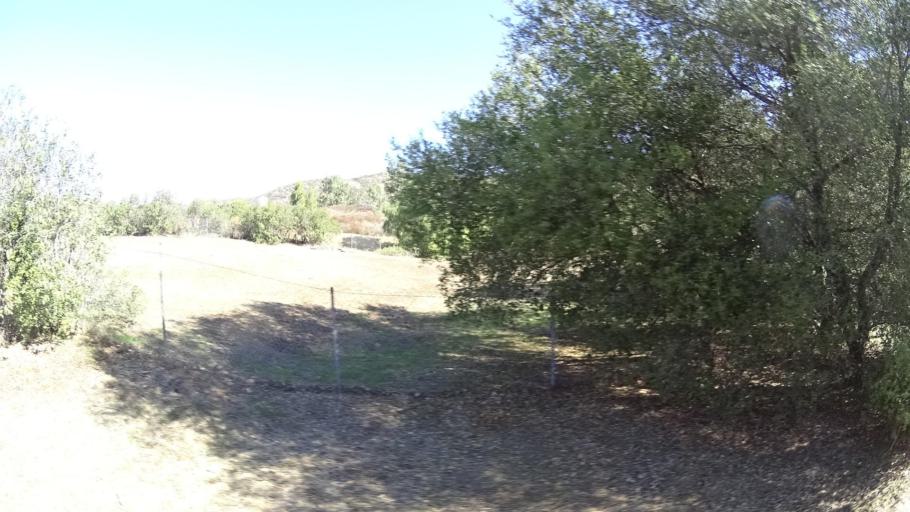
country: US
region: California
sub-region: San Diego County
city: Jamul
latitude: 32.7221
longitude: -116.8058
